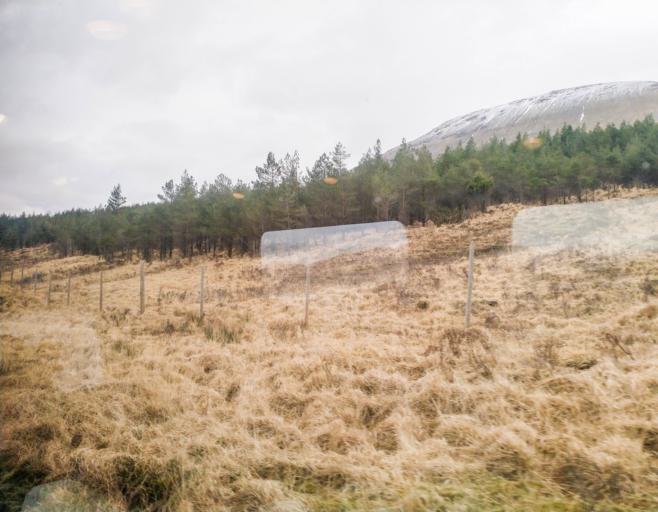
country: GB
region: Scotland
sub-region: Highland
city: Spean Bridge
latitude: 56.5267
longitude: -4.7634
